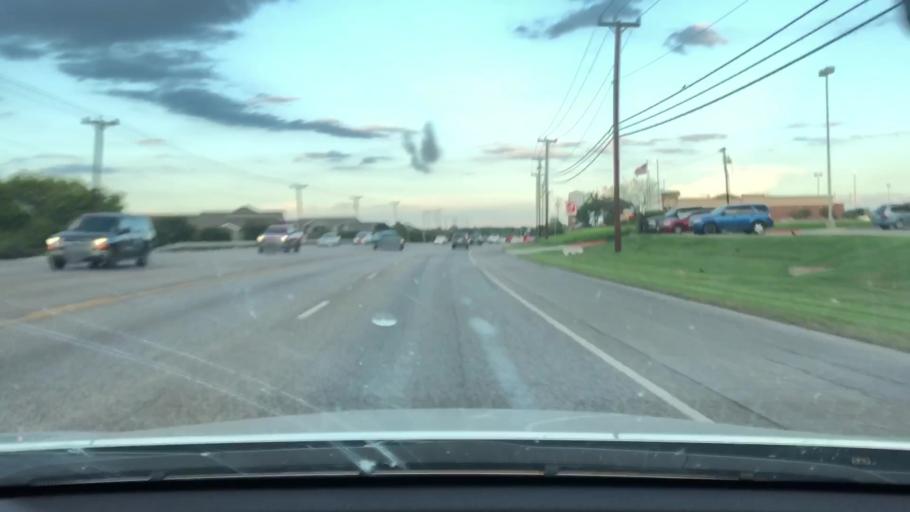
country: US
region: Texas
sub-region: Bexar County
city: Kirby
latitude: 29.4848
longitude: -98.3518
